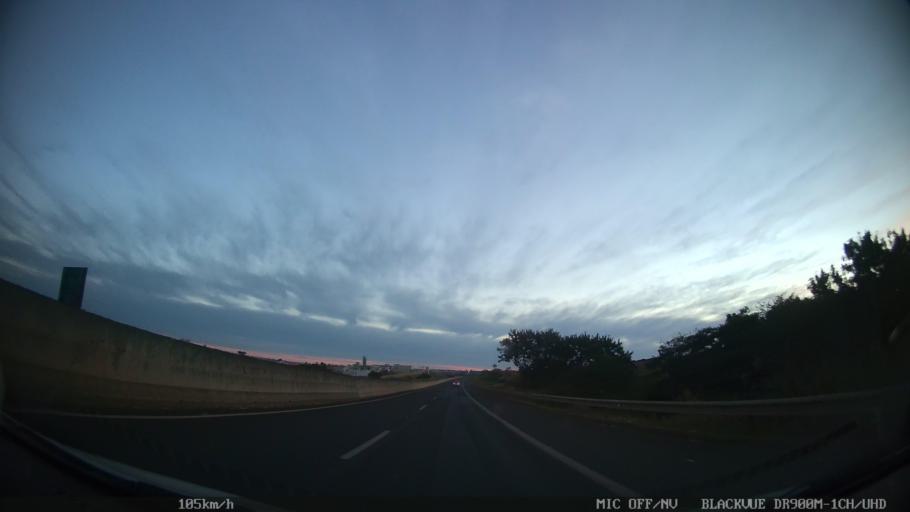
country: BR
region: Sao Paulo
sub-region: Catanduva
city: Catanduva
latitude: -21.1131
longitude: -48.9727
